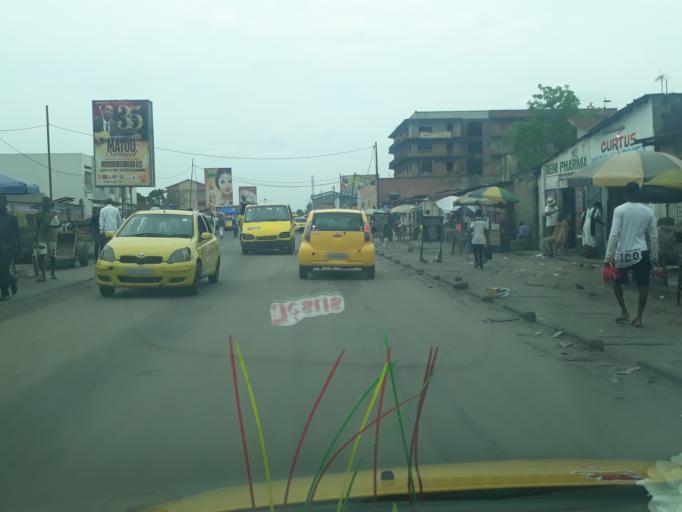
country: CD
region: Kinshasa
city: Kinshasa
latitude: -4.3546
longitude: 15.2992
